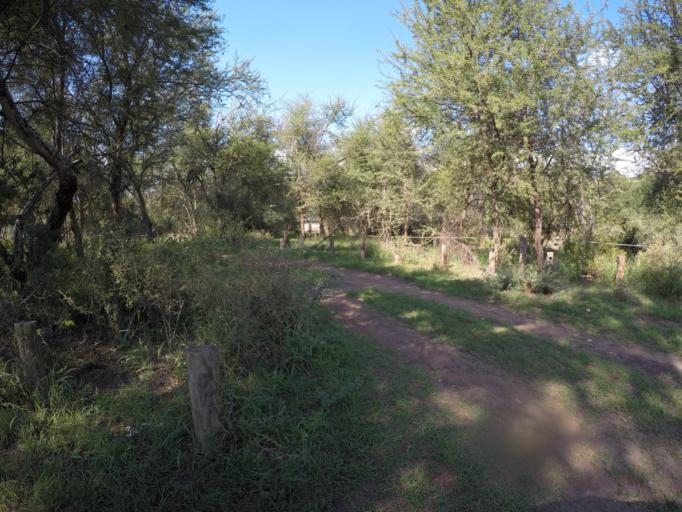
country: ZA
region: Eastern Cape
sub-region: Cacadu District Municipality
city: Kareedouw
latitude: -33.6672
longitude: 24.3842
